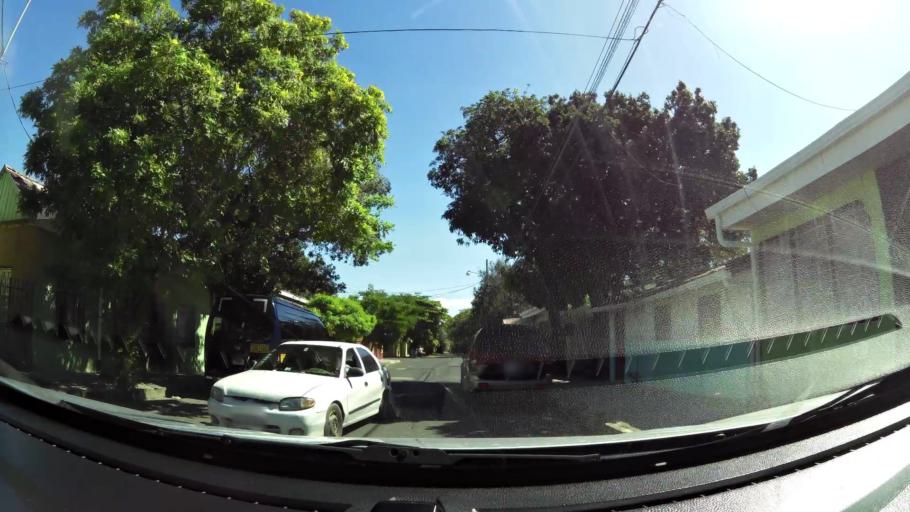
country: CR
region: Guanacaste
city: Liberia
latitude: 10.6329
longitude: -85.4335
